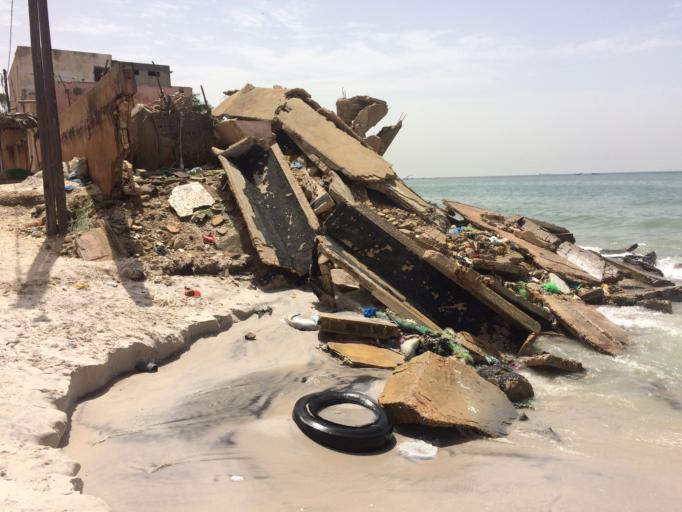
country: SN
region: Dakar
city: Pikine
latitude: 14.7320
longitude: -17.3326
